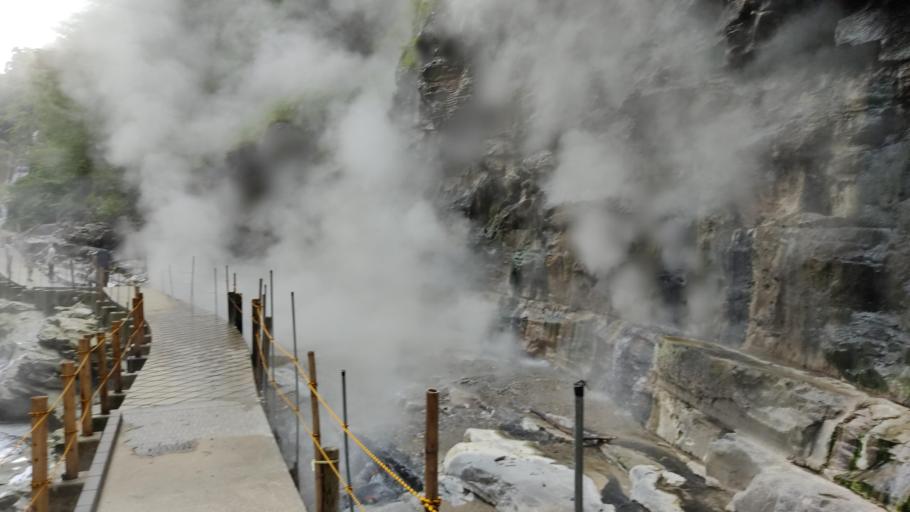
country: JP
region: Akita
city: Yuzawa
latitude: 39.0115
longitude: 140.6610
